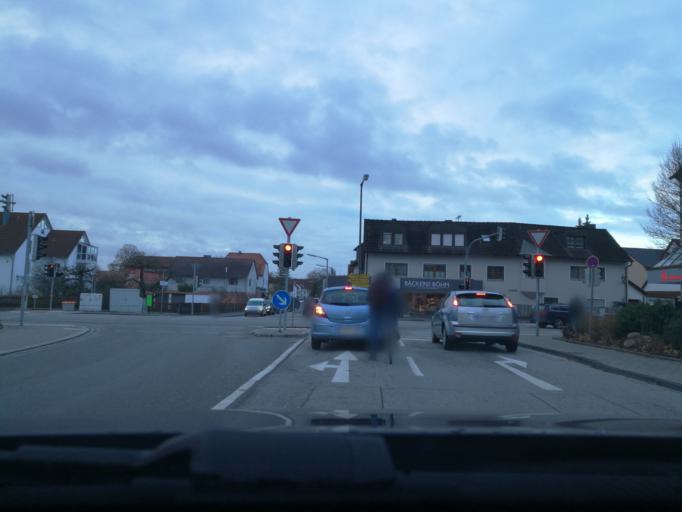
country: DE
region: Bavaria
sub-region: Regierungsbezirk Mittelfranken
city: Uttenreuth
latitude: 49.5973
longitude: 11.0742
